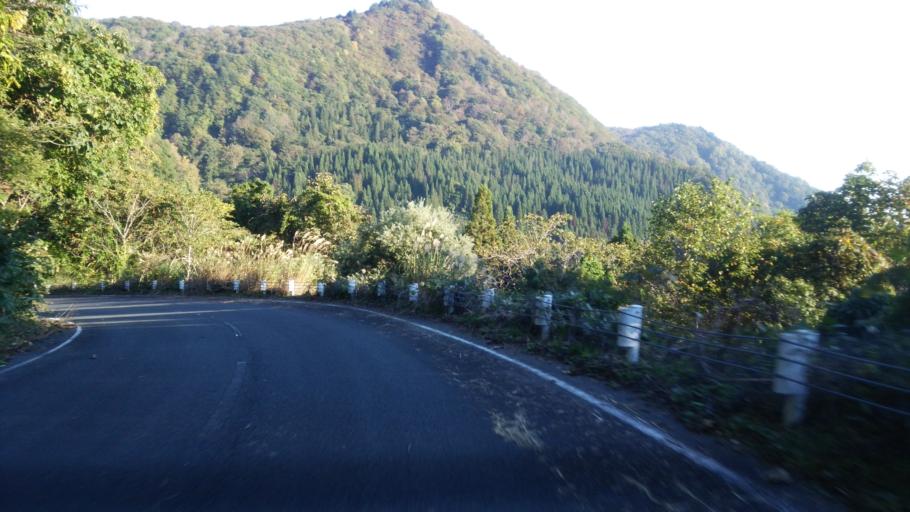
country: JP
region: Fukushima
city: Kitakata
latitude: 37.4115
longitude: 139.7654
